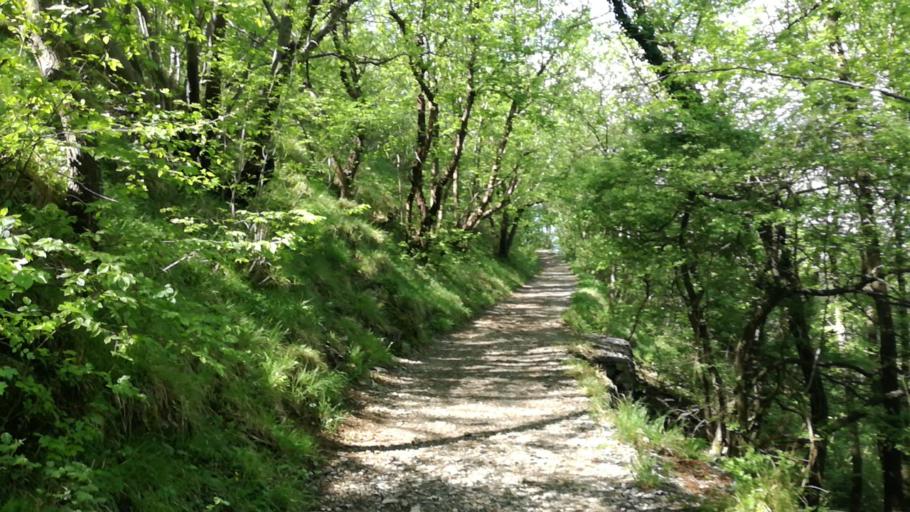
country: IT
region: Liguria
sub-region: Provincia di Genova
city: Genoa
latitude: 44.4475
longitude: 8.9379
